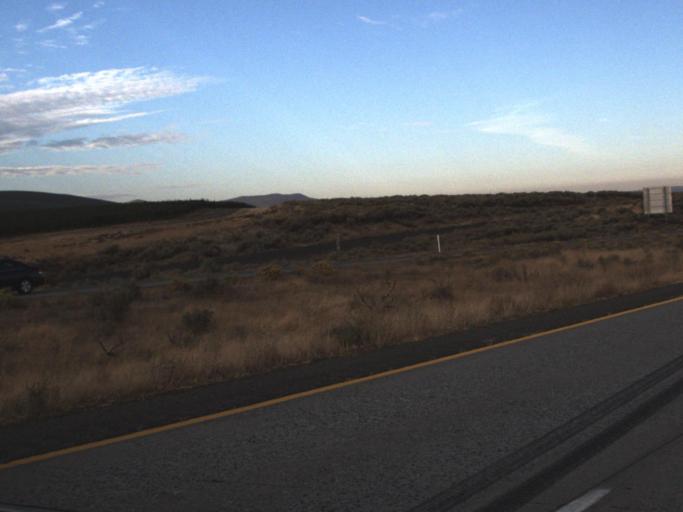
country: US
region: Washington
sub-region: Benton County
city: West Richland
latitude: 46.2575
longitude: -119.3836
